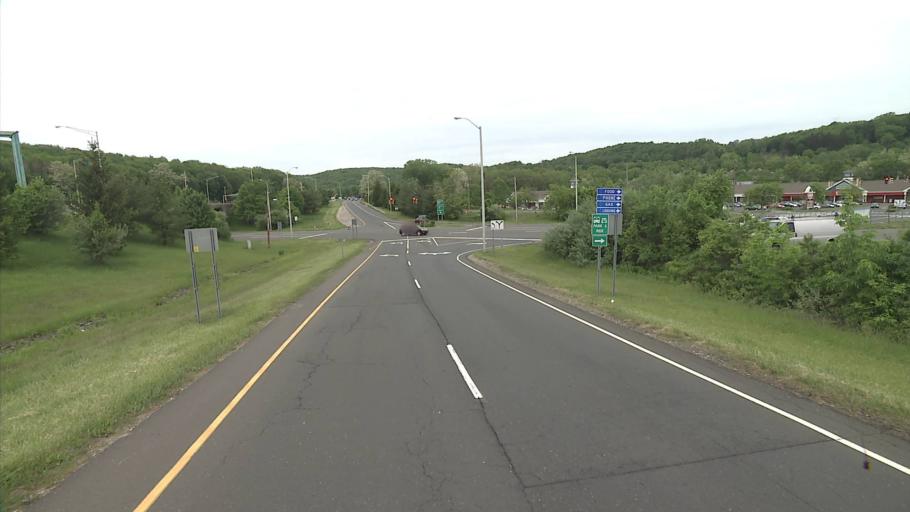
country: US
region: New York
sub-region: Putnam County
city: Peach Lake
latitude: 41.3910
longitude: -73.5207
